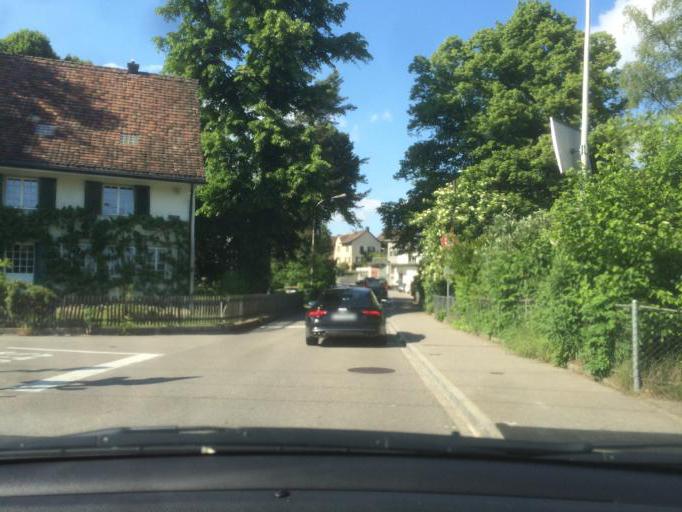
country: CH
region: Zurich
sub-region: Bezirk Uster
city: Uster
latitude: 47.3471
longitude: 8.7269
